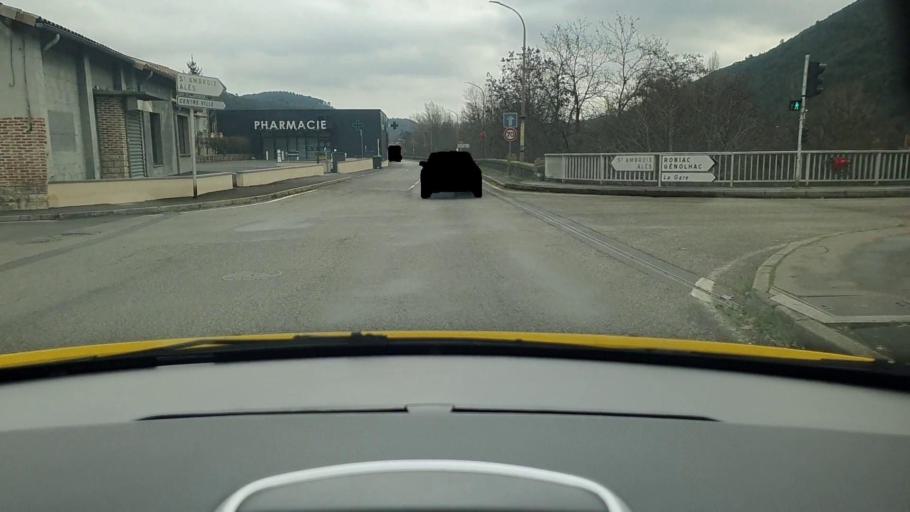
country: FR
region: Languedoc-Roussillon
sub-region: Departement du Gard
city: Besseges
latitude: 44.2896
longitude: 4.1010
